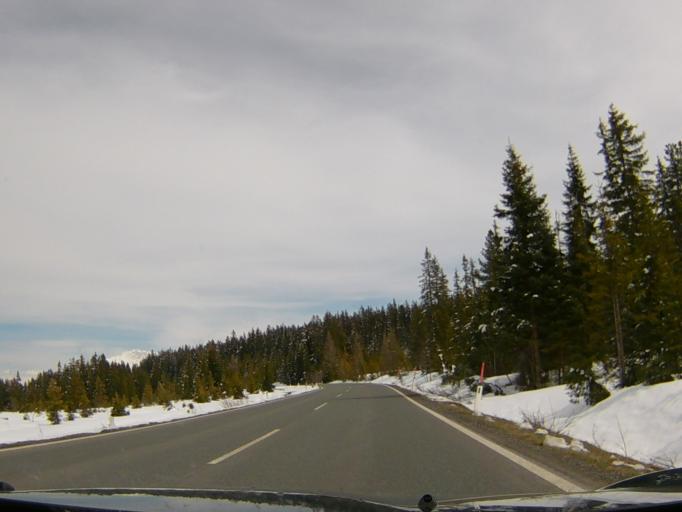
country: AT
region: Salzburg
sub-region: Politischer Bezirk Zell am See
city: Krimml
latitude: 47.2406
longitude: 12.1443
